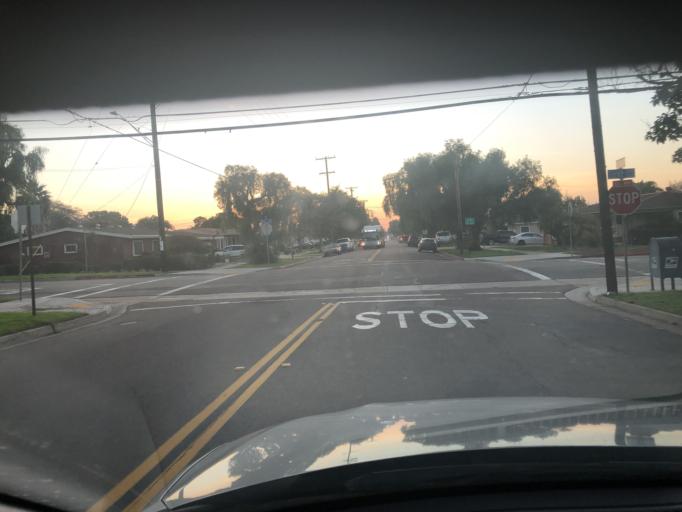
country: US
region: California
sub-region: San Diego County
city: Chula Vista
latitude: 32.6437
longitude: -117.0714
